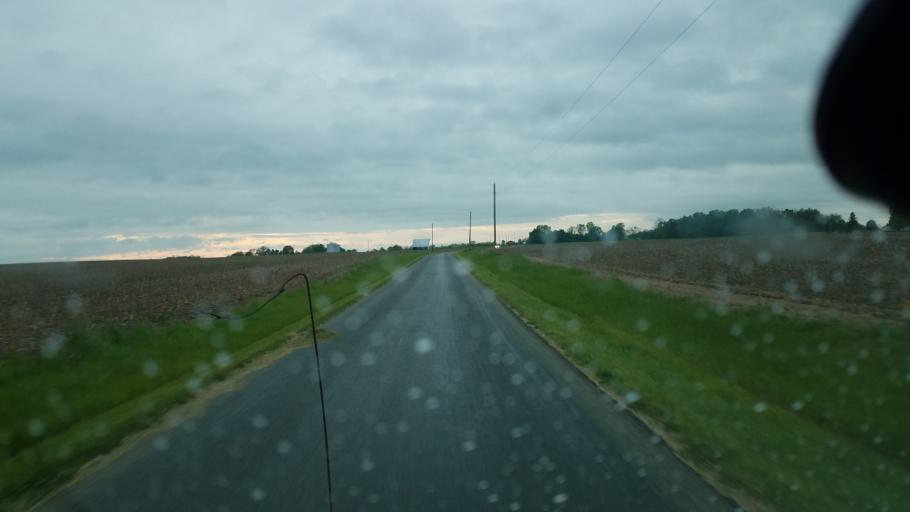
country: US
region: Ohio
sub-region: Highland County
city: Greenfield
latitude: 39.3295
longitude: -83.4310
